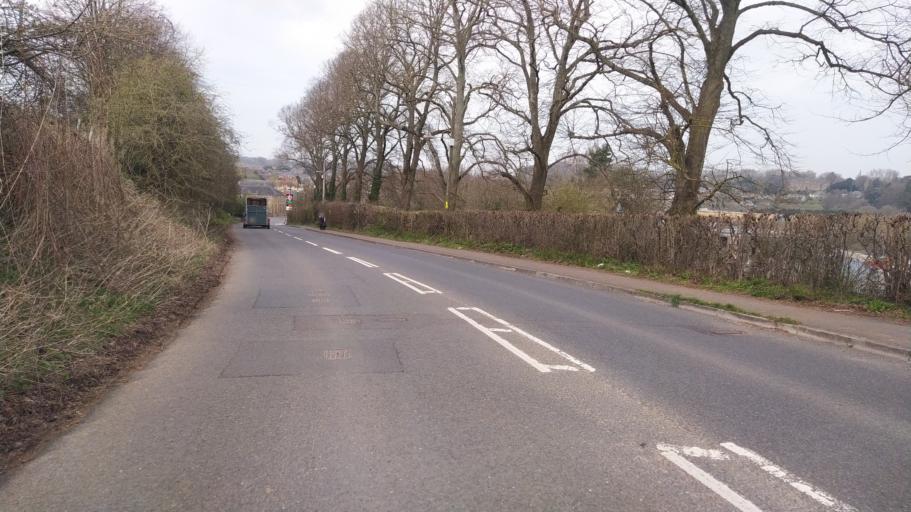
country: GB
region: England
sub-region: Somerset
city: Crewkerne
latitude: 50.8787
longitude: -2.7816
